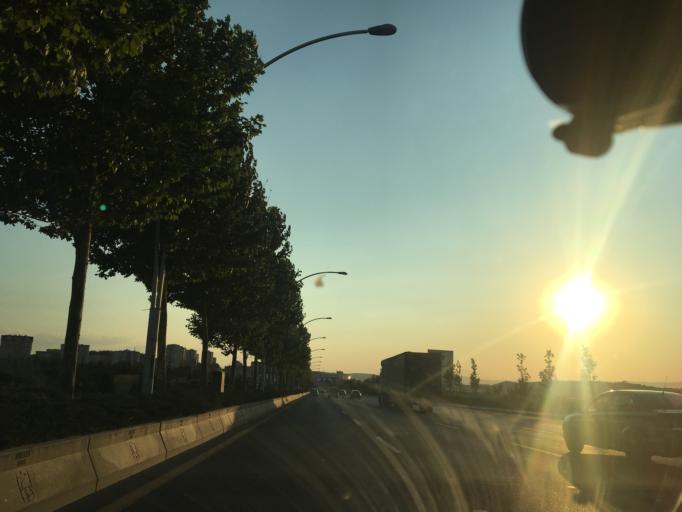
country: TR
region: Ankara
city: Batikent
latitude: 39.9062
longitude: 32.7214
